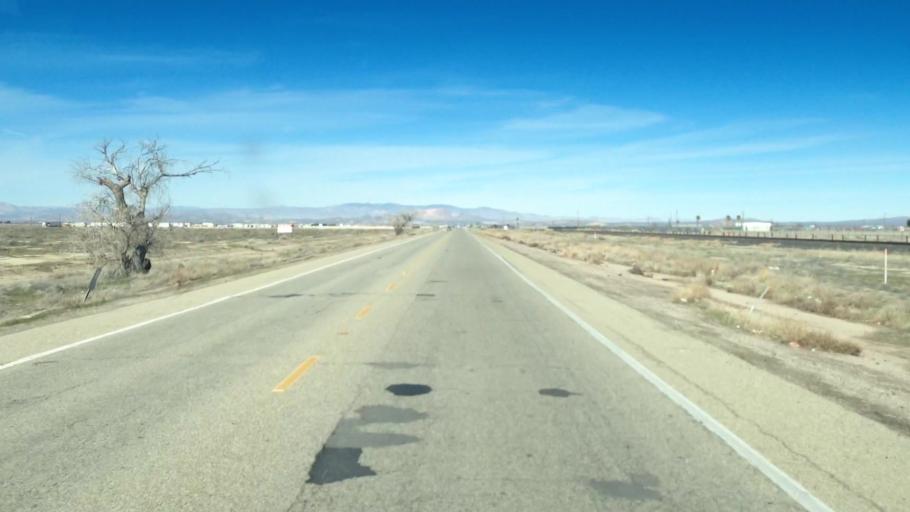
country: US
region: California
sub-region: Los Angeles County
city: Lancaster
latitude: 34.7283
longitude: -118.1414
